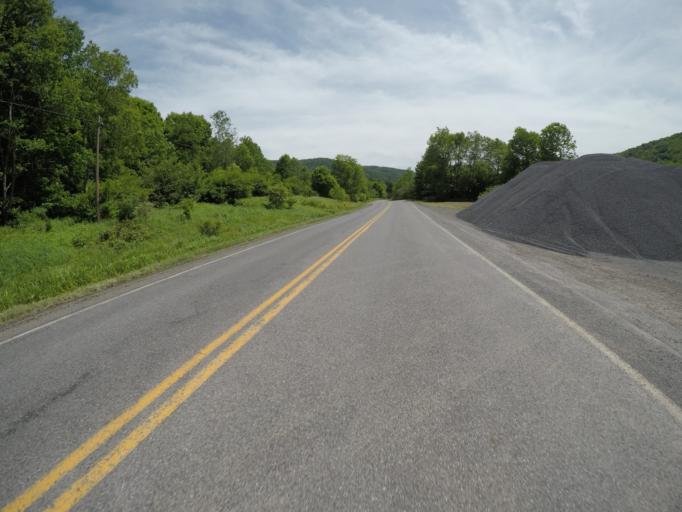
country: US
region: New York
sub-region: Delaware County
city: Delhi
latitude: 42.1553
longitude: -74.7979
